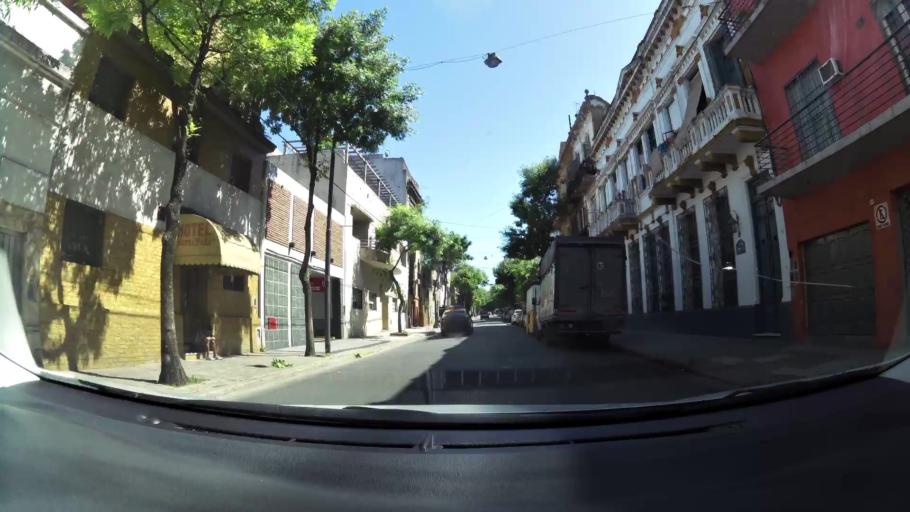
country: AR
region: Buenos Aires F.D.
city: Buenos Aires
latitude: -34.6259
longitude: -58.3873
